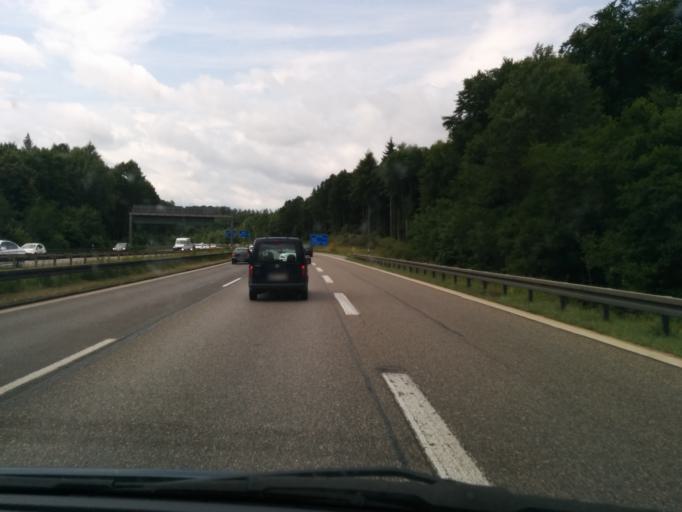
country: DE
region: Baden-Wuerttemberg
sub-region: Regierungsbezirk Stuttgart
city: Sindelfingen
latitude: 48.7231
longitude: 9.0616
